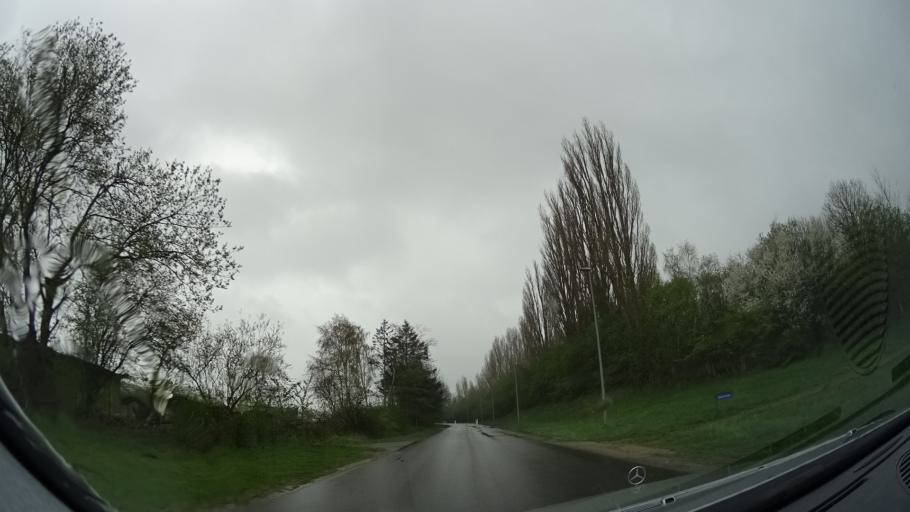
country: DK
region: Zealand
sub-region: Holbaek Kommune
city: Holbaek
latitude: 55.7204
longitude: 11.7572
